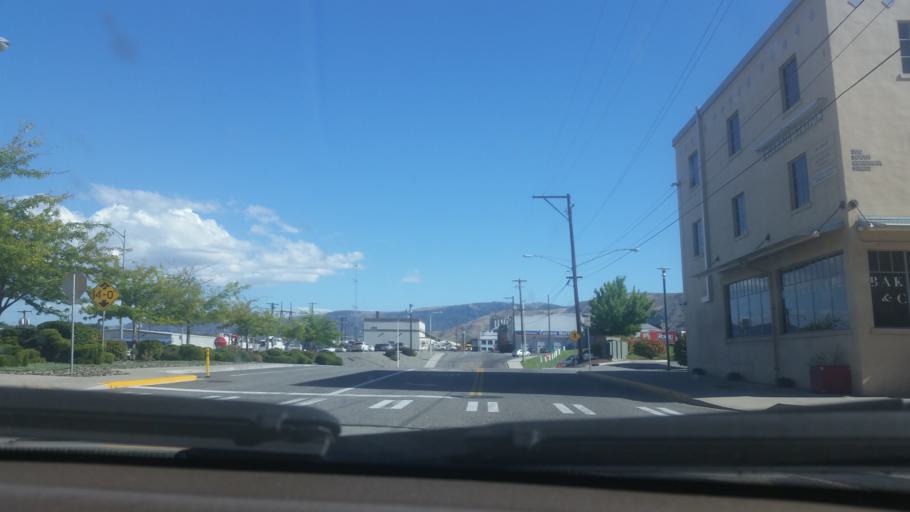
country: US
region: Washington
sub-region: Chelan County
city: Wenatchee
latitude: 47.4215
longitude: -120.3073
